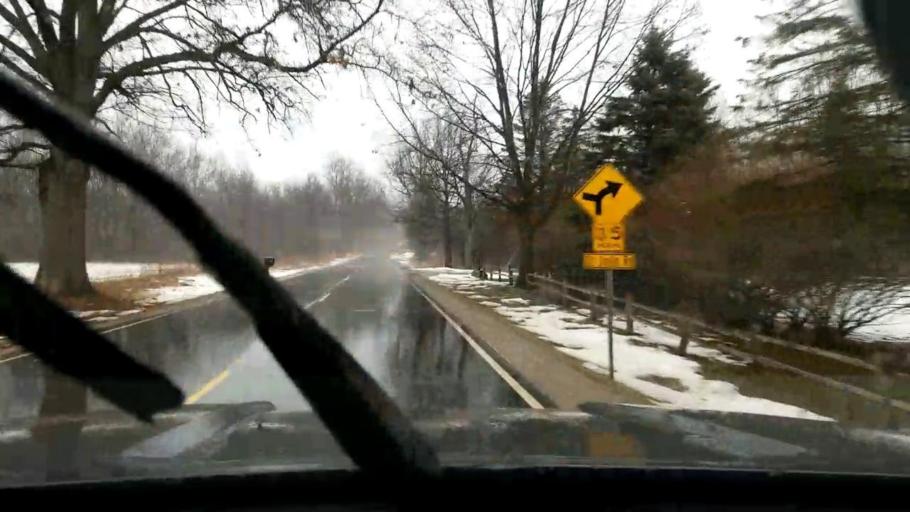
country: US
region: Michigan
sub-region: Jackson County
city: Michigan Center
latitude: 42.3111
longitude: -84.3093
